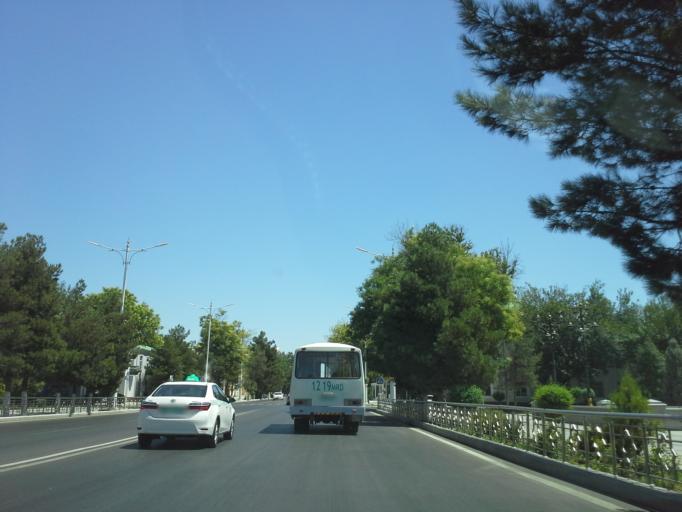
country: TM
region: Ahal
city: Ashgabat
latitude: 37.9471
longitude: 58.3785
